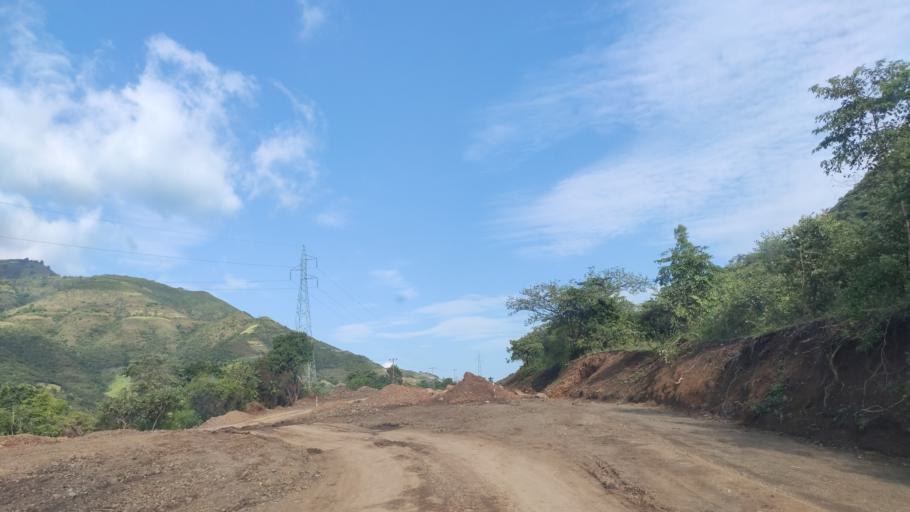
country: ET
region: Southern Nations, Nationalities, and People's Region
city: Arba Minch'
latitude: 6.4257
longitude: 37.3396
